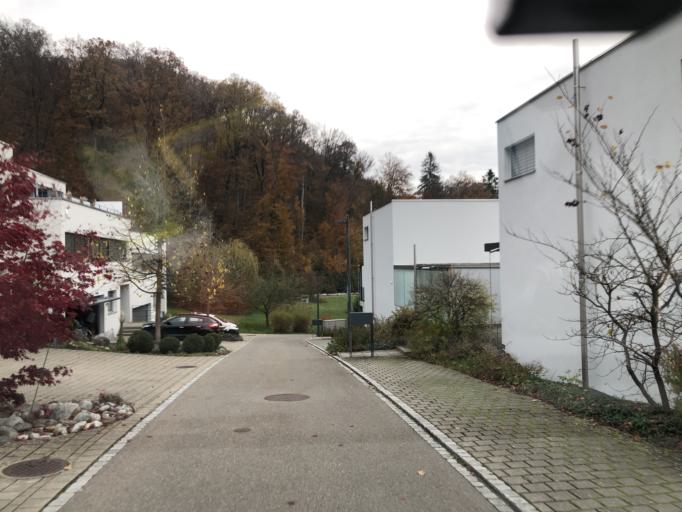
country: CH
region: Aargau
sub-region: Bezirk Baden
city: Birmenstorf
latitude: 47.4620
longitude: 8.2773
